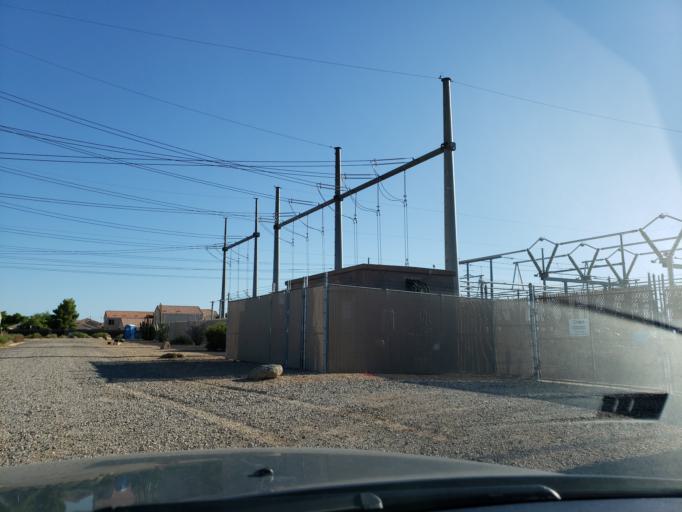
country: US
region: Arizona
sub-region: Maricopa County
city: Avondale
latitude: 33.4667
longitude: -112.3142
